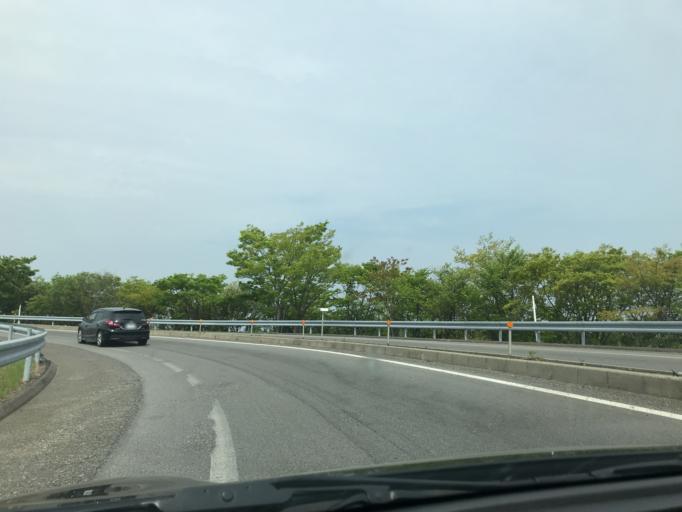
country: JP
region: Niigata
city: Kameda-honcho
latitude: 37.8795
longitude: 139.0834
